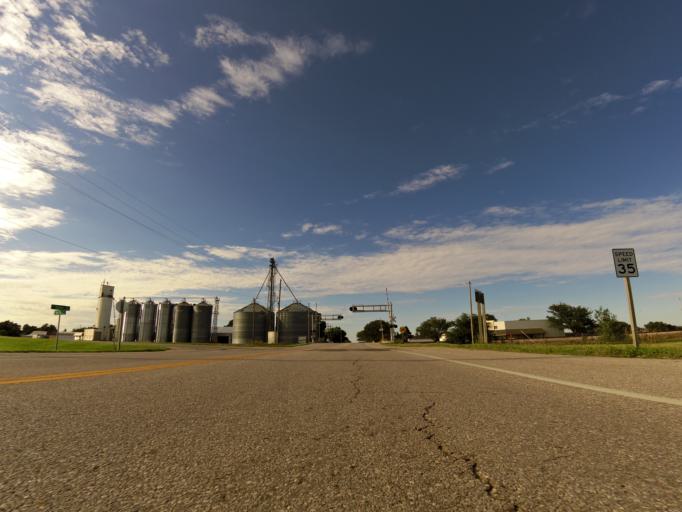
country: US
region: Kansas
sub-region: Reno County
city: Haven
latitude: 37.9378
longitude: -97.8667
